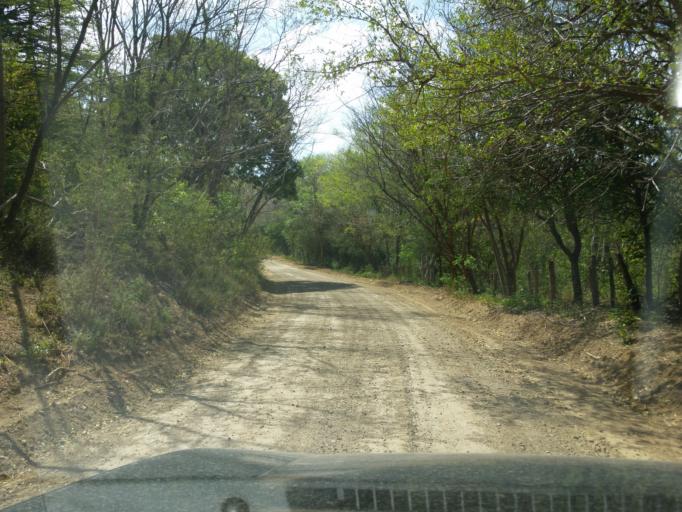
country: NI
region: Rivas
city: San Juan del Sur
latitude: 11.1330
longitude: -85.7808
